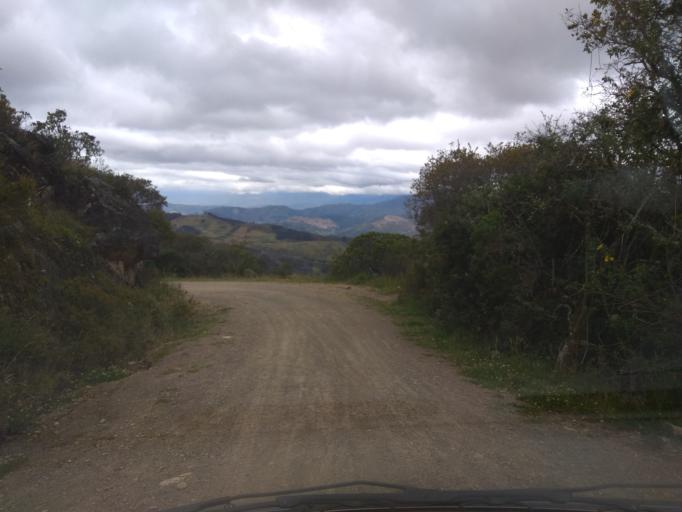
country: CO
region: Boyaca
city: Mongui
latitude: 5.7350
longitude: -72.8308
